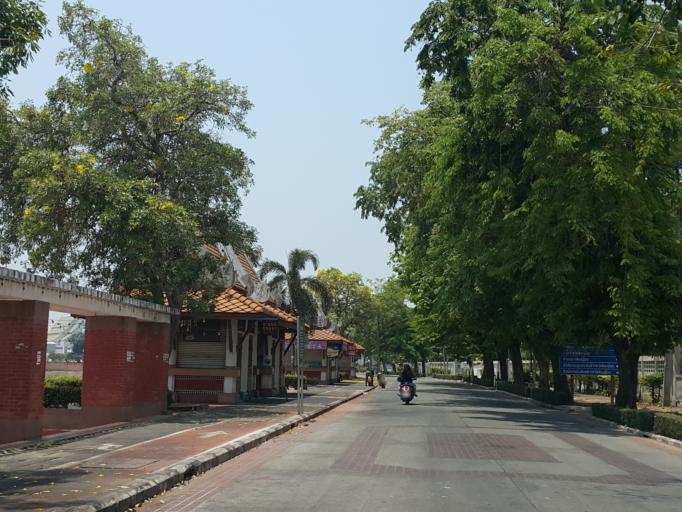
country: TH
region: Phitsanulok
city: Phitsanulok
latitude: 16.8225
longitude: 100.2589
